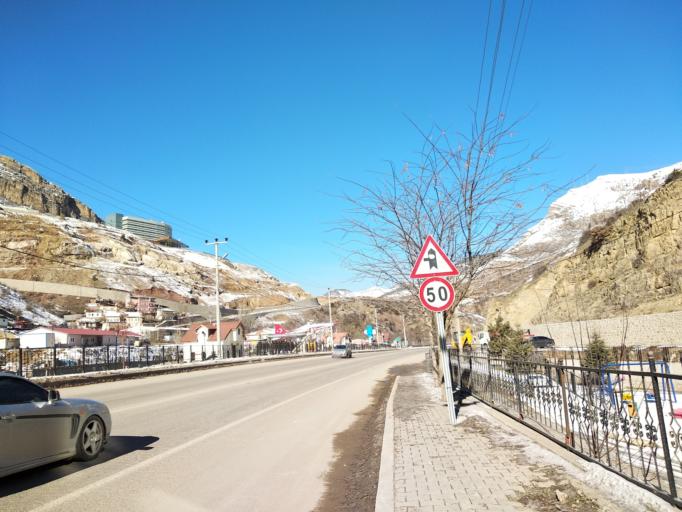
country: TR
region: Gumushane
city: Gumushkhane
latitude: 40.4388
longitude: 39.5045
